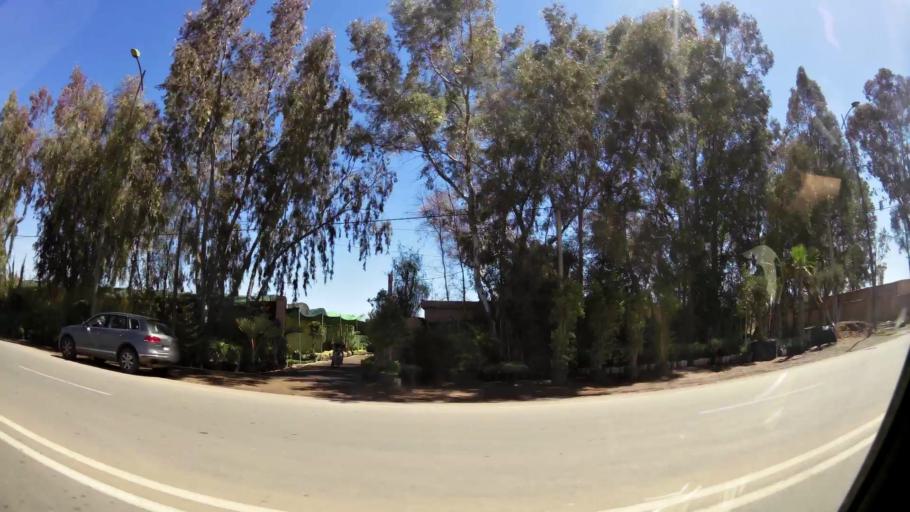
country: MA
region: Marrakech-Tensift-Al Haouz
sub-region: Marrakech
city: Marrakesh
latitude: 31.5650
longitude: -7.9800
